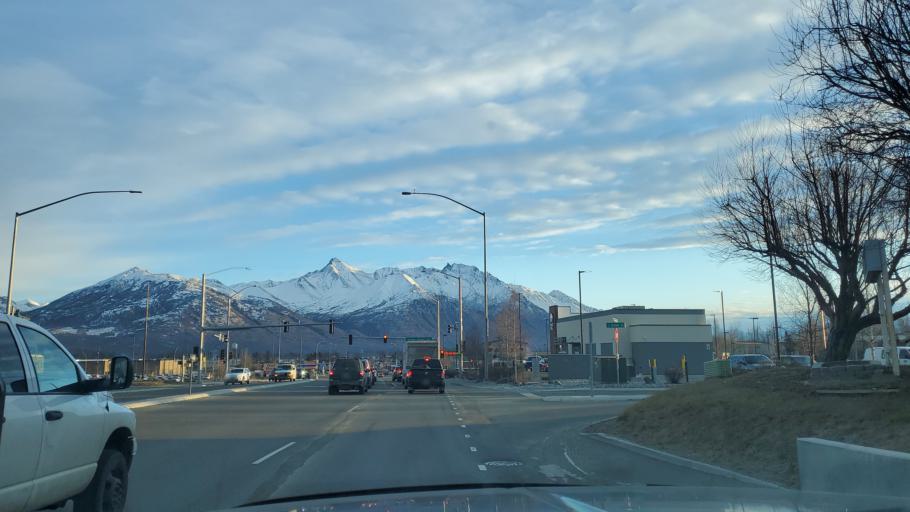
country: US
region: Alaska
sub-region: Matanuska-Susitna Borough
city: Palmer
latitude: 61.5994
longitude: -149.1289
